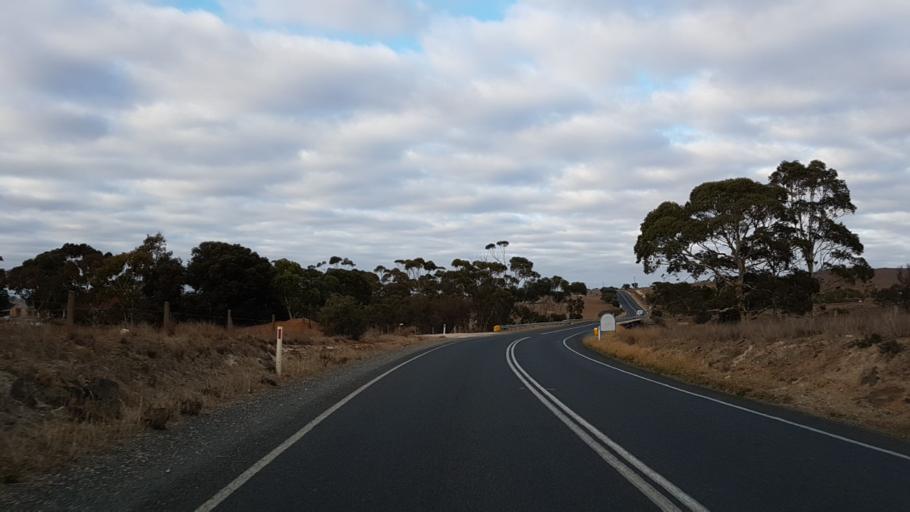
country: AU
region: South Australia
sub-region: Mount Barker
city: Callington
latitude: -35.1380
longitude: 139.0292
